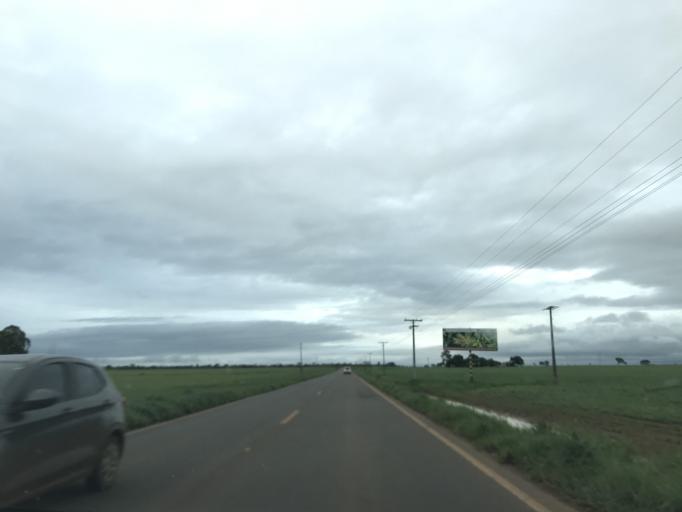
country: BR
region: Goias
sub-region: Luziania
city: Luziania
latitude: -16.3028
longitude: -48.0110
